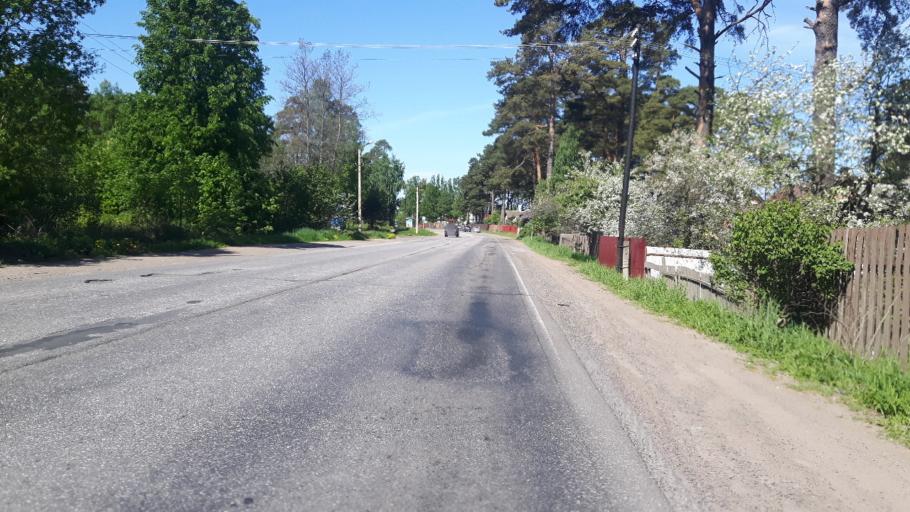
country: RU
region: Leningrad
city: Lebyazh'ye
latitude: 59.9602
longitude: 29.4344
